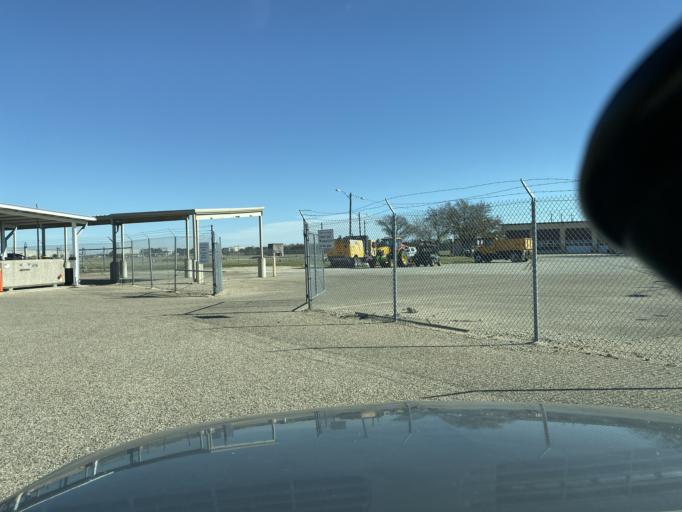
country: US
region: Texas
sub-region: Travis County
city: Hornsby Bend
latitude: 30.1885
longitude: -97.6704
